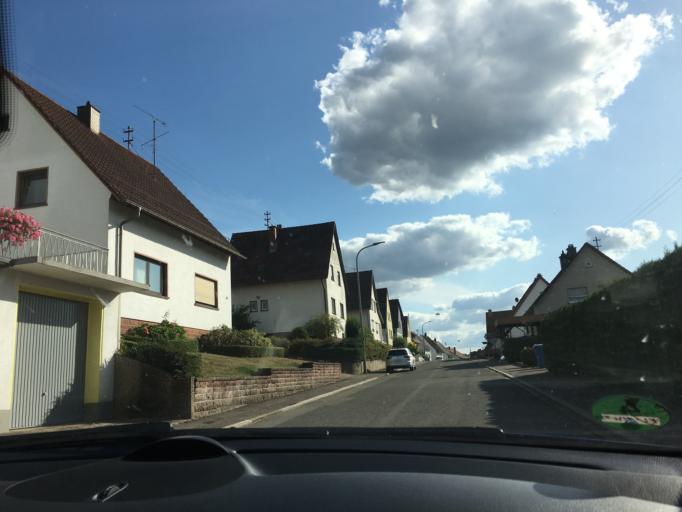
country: DE
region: Rheinland-Pfalz
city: Schopp
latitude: 49.3506
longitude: 7.6896
